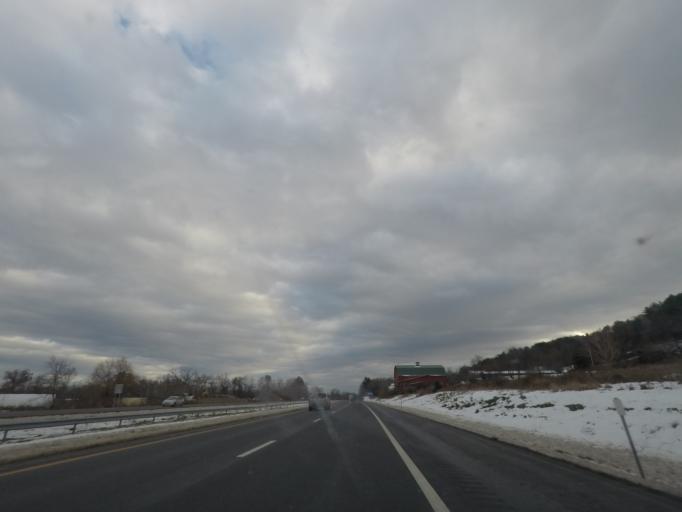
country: US
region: New York
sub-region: Ulster County
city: Lincoln Park
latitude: 41.9633
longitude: -74.0152
